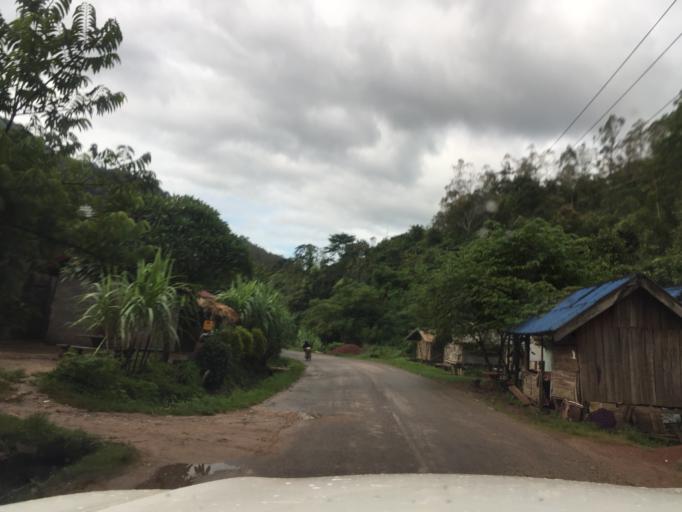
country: LA
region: Oudomxai
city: Muang La
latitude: 20.8142
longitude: 102.0915
